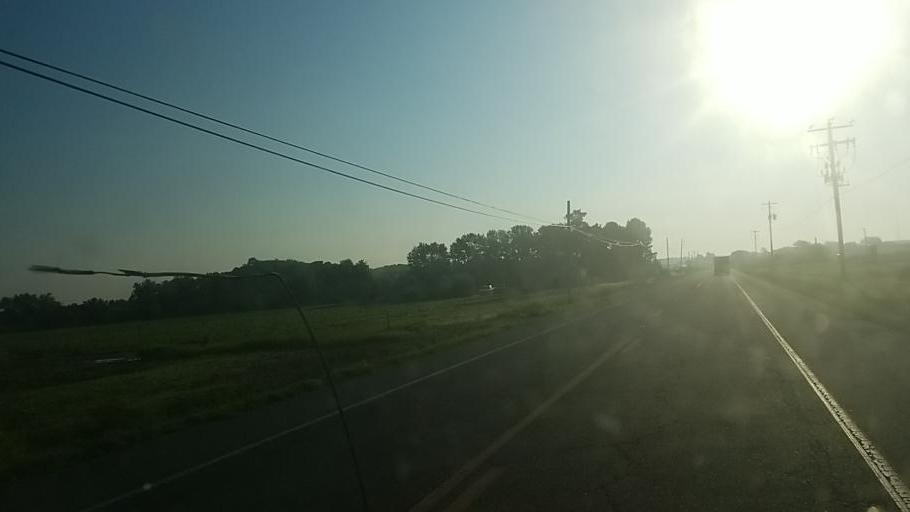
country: US
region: Delaware
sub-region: Sussex County
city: Selbyville
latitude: 38.4633
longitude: -75.1820
